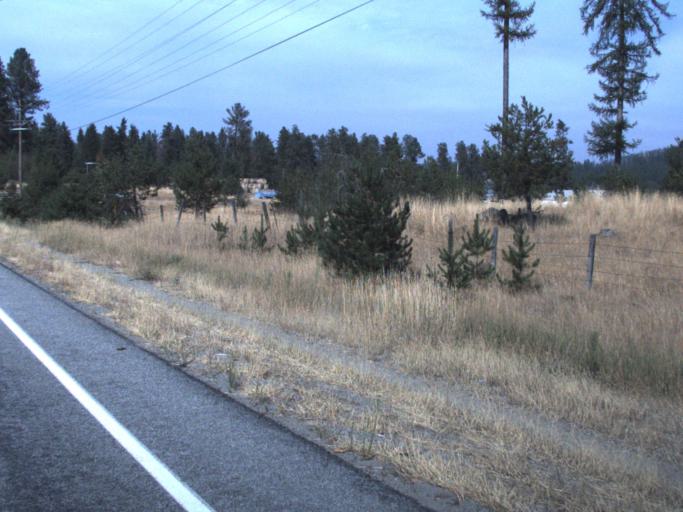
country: US
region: Washington
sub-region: Pend Oreille County
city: Newport
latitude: 48.1749
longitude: -117.3015
